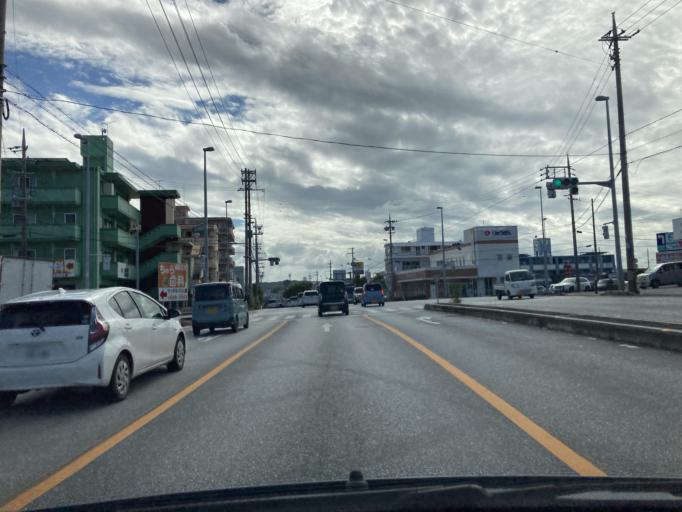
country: JP
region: Okinawa
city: Tomigusuku
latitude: 26.1629
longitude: 127.7237
